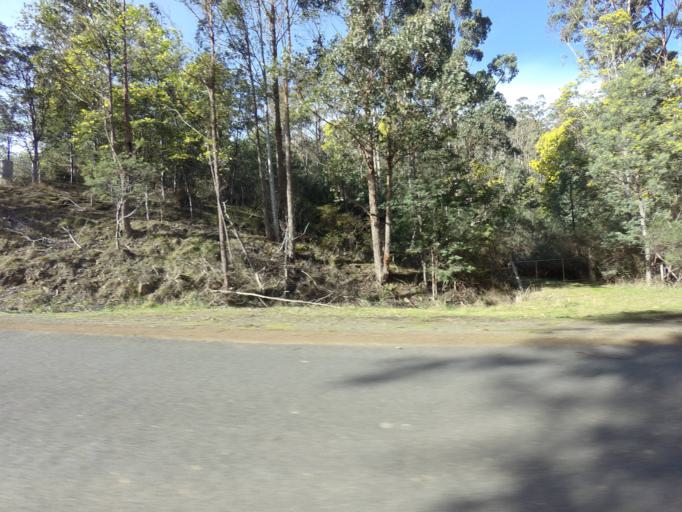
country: AU
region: Tasmania
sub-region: Huon Valley
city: Cygnet
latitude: -43.1765
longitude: 147.1503
